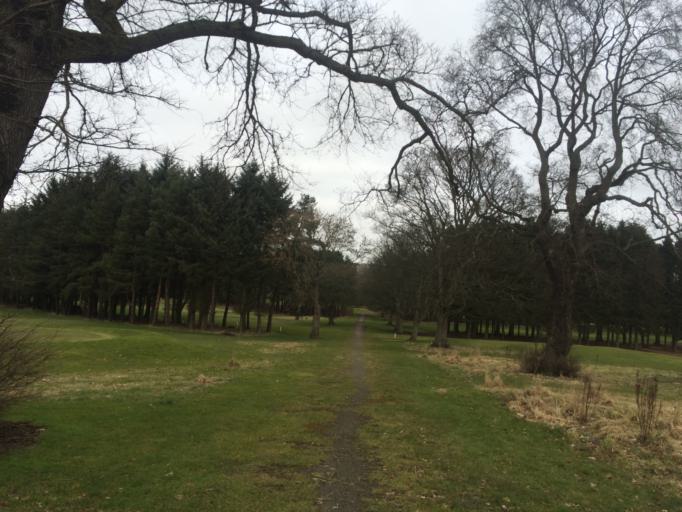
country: GB
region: Scotland
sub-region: Dundee City
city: Dundee
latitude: 56.4827
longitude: -2.9679
